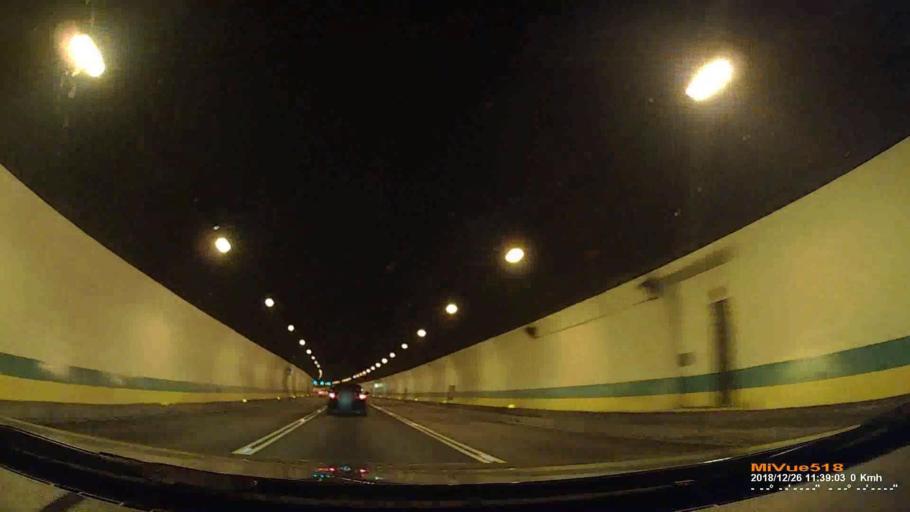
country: TW
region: Taipei
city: Taipei
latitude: 24.9871
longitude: 121.5893
